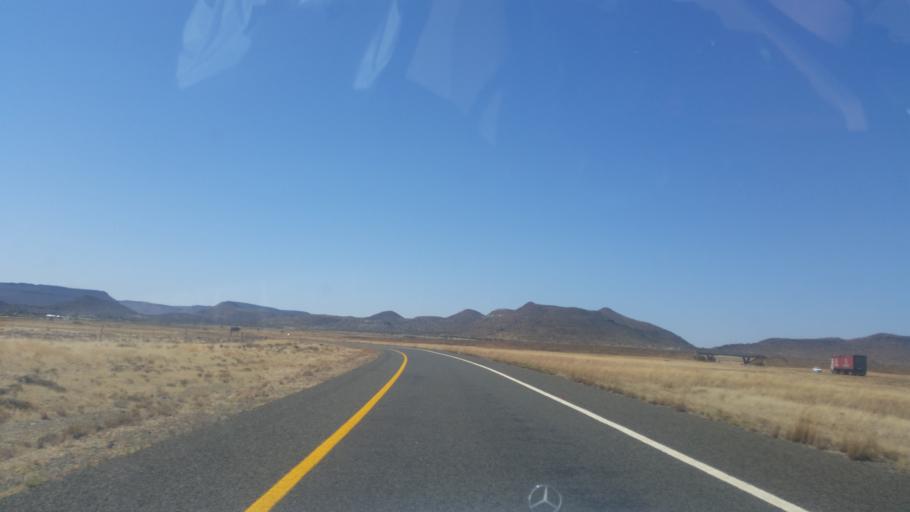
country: ZA
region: Northern Cape
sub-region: Pixley ka Seme District Municipality
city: Colesberg
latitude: -30.5532
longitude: 25.4891
